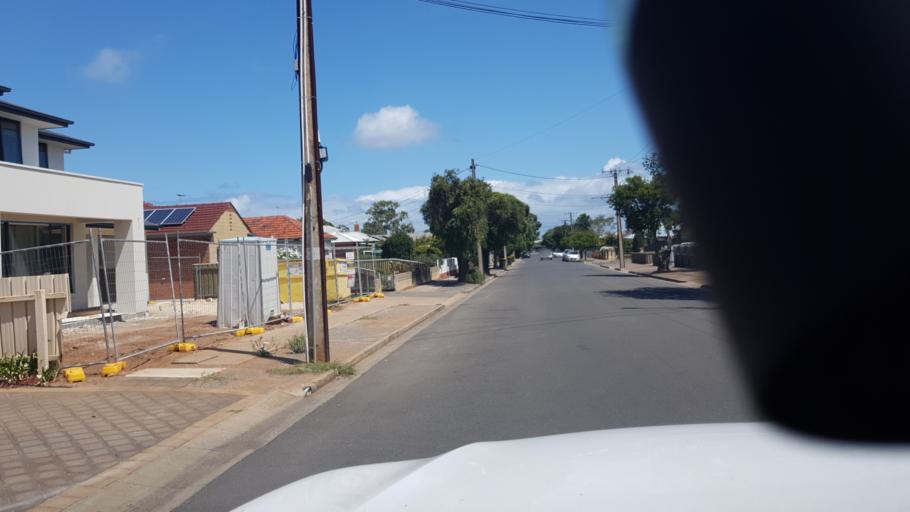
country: AU
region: South Australia
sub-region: Holdfast Bay
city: North Brighton
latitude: -35.0078
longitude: 138.5260
